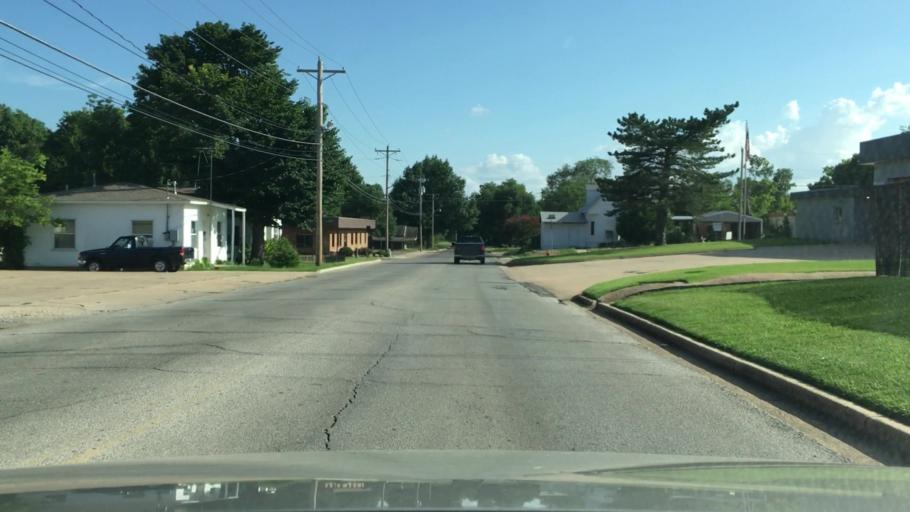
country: US
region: Oklahoma
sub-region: Cherokee County
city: Tahlequah
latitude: 35.9102
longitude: -94.9709
